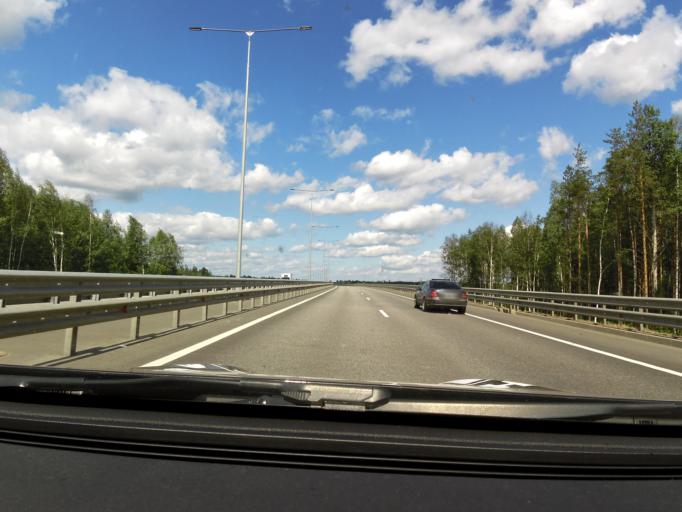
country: RU
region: Tverskaya
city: Vydropuzhsk
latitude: 57.2634
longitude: 34.8736
